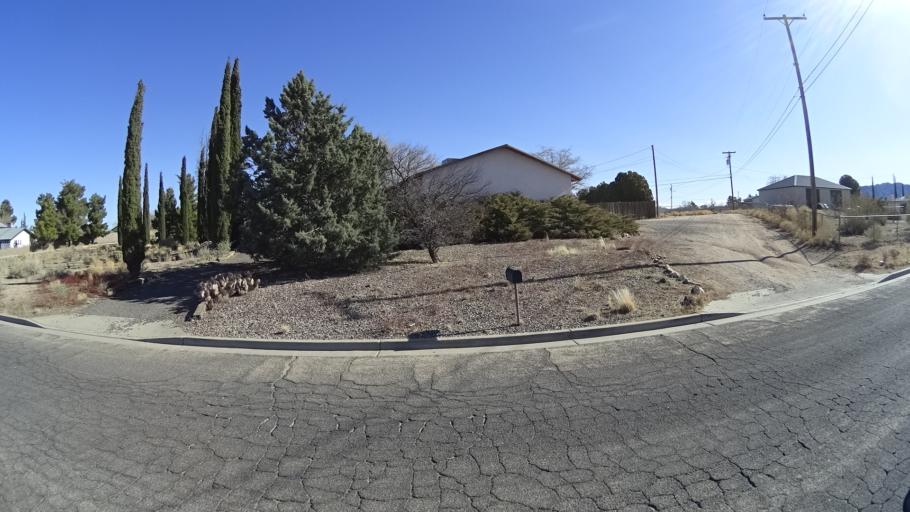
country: US
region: Arizona
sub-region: Mohave County
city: Kingman
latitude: 35.1984
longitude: -114.0062
